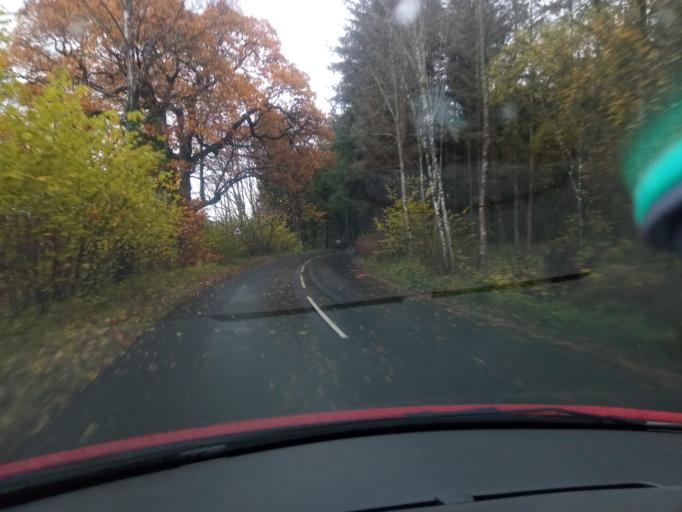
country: GB
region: England
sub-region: Northumberland
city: Birtley
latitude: 55.1019
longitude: -2.2291
